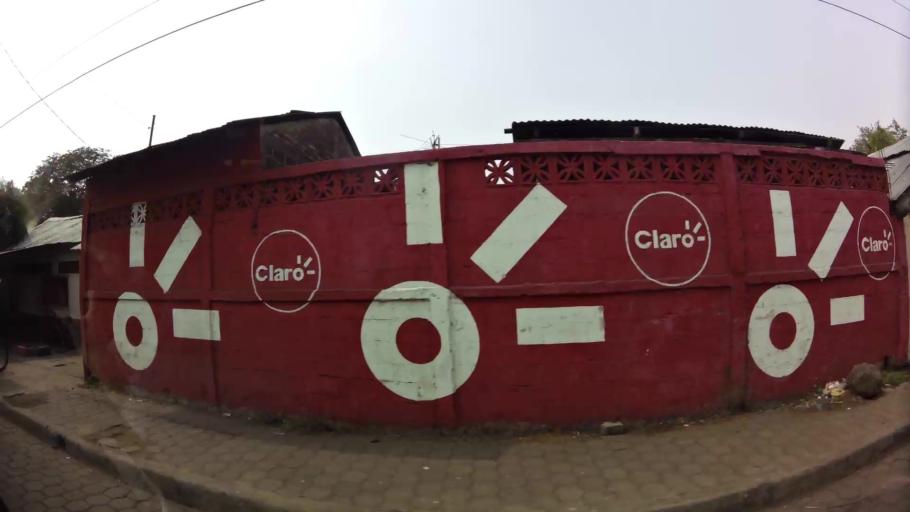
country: NI
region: Chinandega
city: Chinandega
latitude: 12.6300
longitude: -87.1374
